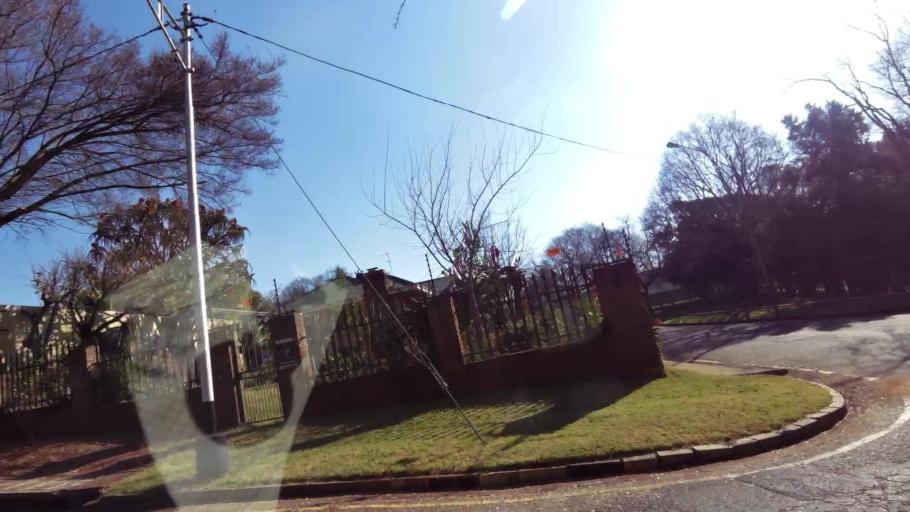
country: ZA
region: Gauteng
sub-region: City of Johannesburg Metropolitan Municipality
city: Johannesburg
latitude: -26.1737
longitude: 27.9989
